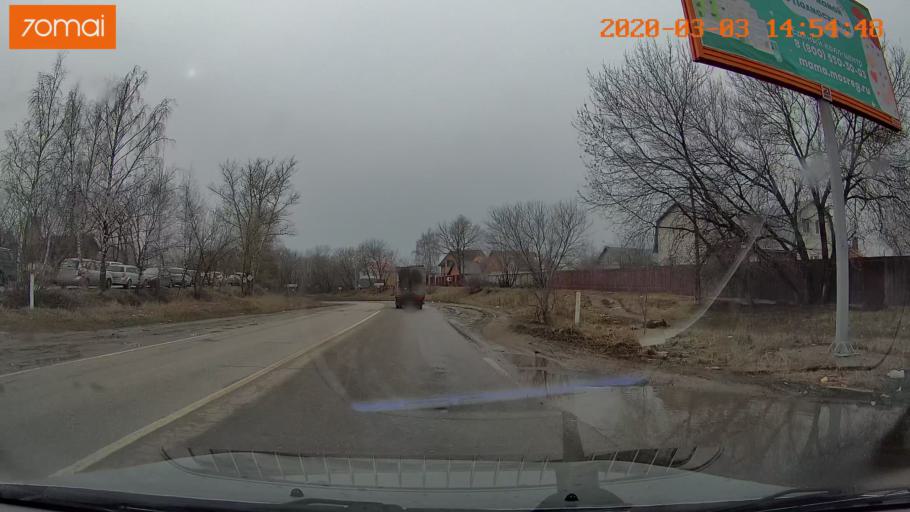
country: RU
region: Moskovskaya
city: Korenevo
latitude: 55.6698
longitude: 38.0000
